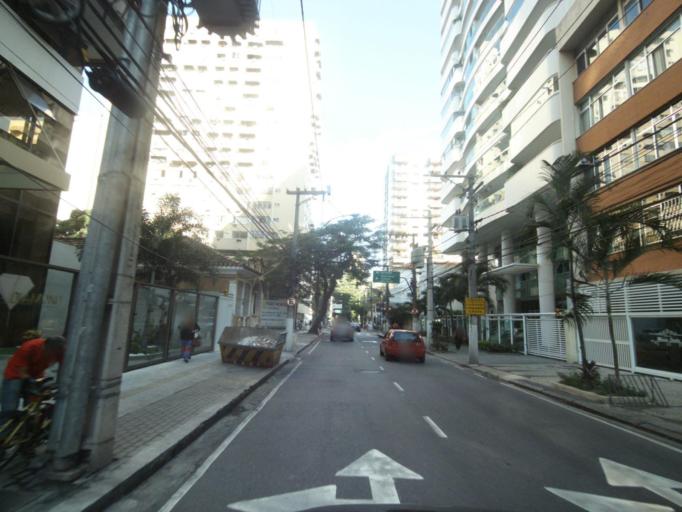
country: BR
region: Rio de Janeiro
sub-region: Niteroi
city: Niteroi
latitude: -22.9023
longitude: -43.1098
